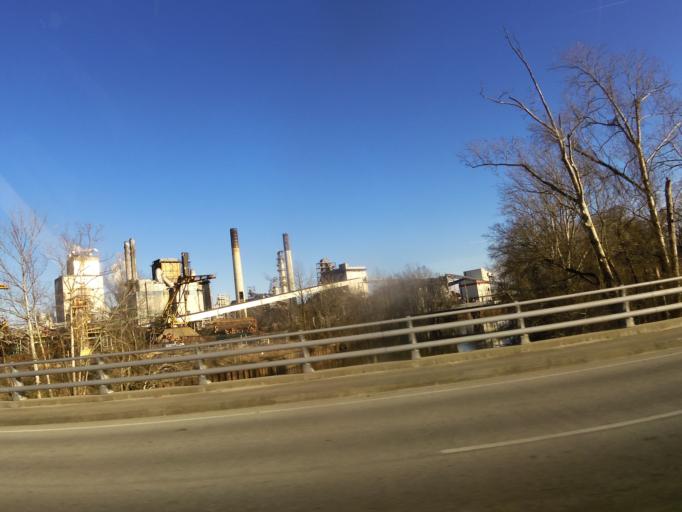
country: US
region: Virginia
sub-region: City of Franklin
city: Franklin
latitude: 36.6809
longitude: -76.9184
